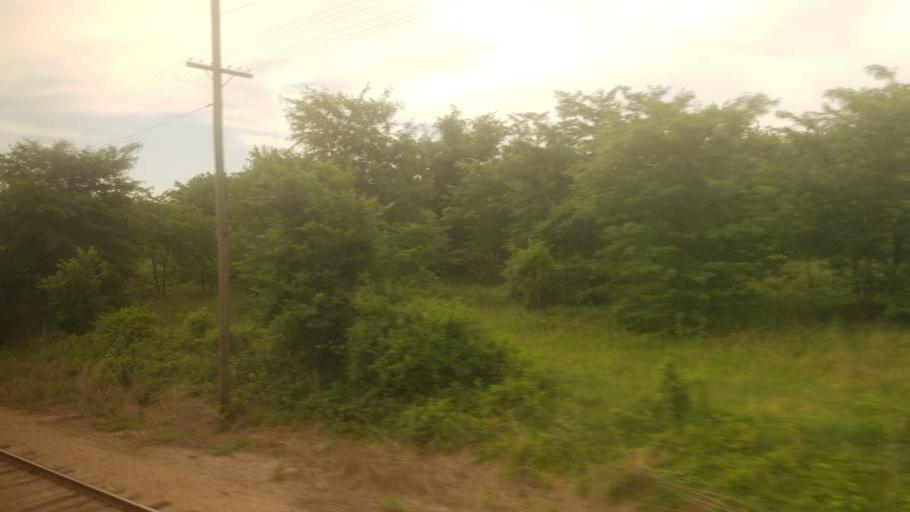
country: US
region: Kansas
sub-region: Shawnee County
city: Topeka
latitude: 39.0597
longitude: -95.5484
